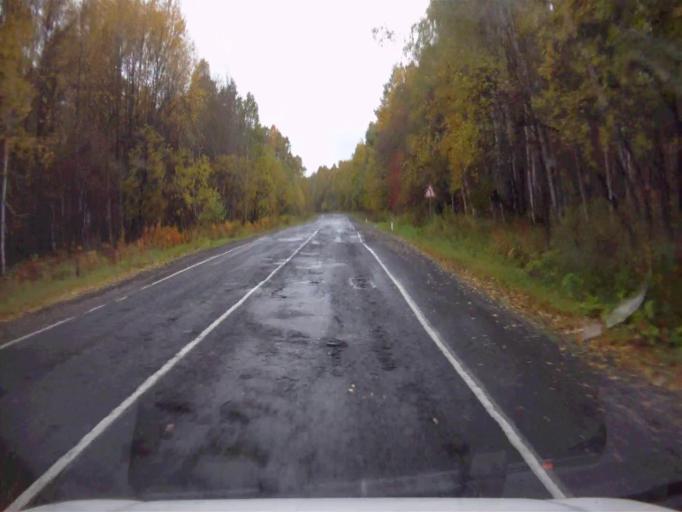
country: RU
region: Chelyabinsk
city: Nizhniy Ufaley
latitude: 56.0544
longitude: 60.0547
